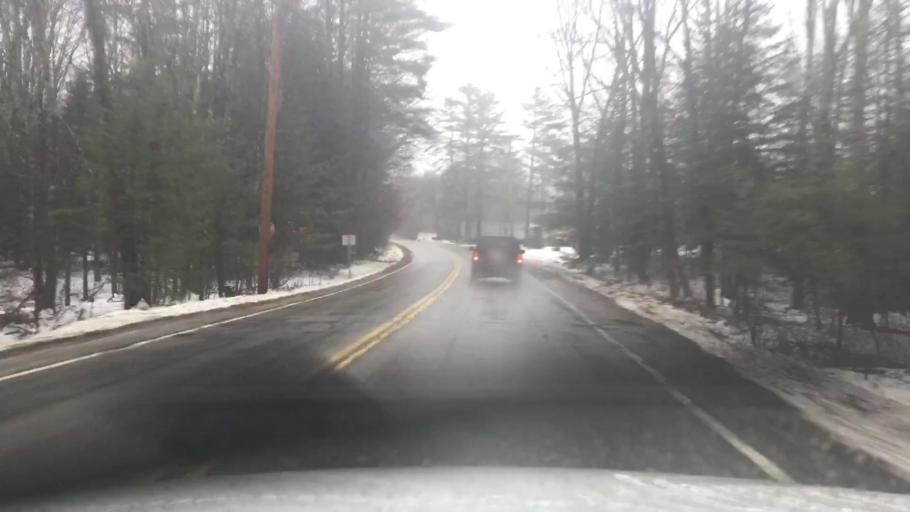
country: US
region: Maine
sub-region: Cumberland County
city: Westbrook
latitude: 43.6352
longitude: -70.3776
